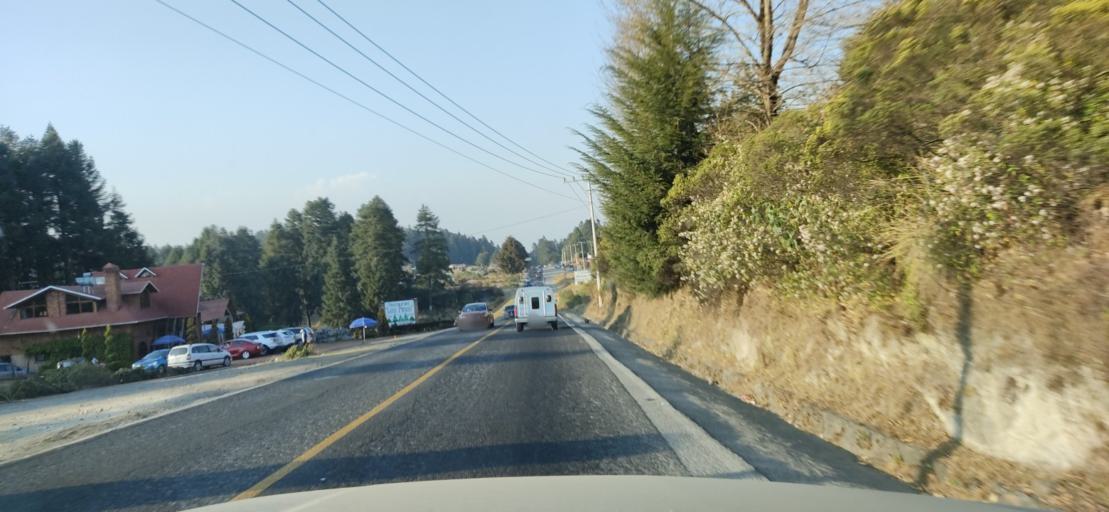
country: MX
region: Mexico
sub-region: Ocoyoacac
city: San Jeronimo Acazulco
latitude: 19.2653
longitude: -99.3766
